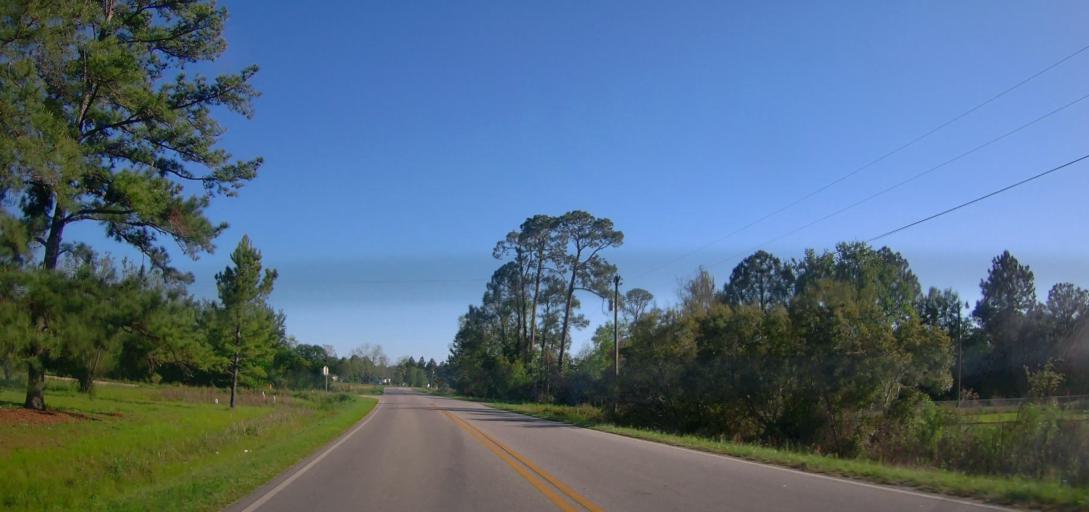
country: US
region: Georgia
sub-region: Ben Hill County
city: Fitzgerald
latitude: 31.7345
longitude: -83.2354
